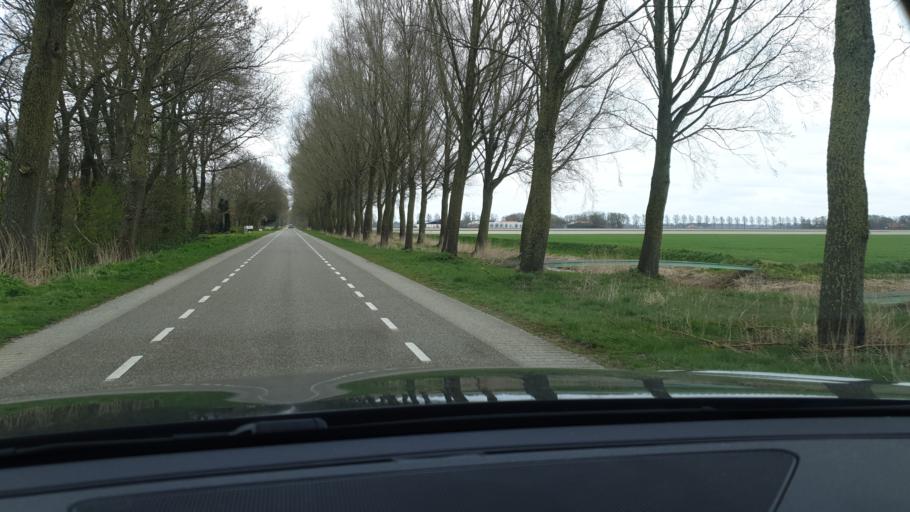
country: NL
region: Friesland
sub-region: Gemeente Lemsterland
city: Lemmer
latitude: 52.7854
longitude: 5.6322
